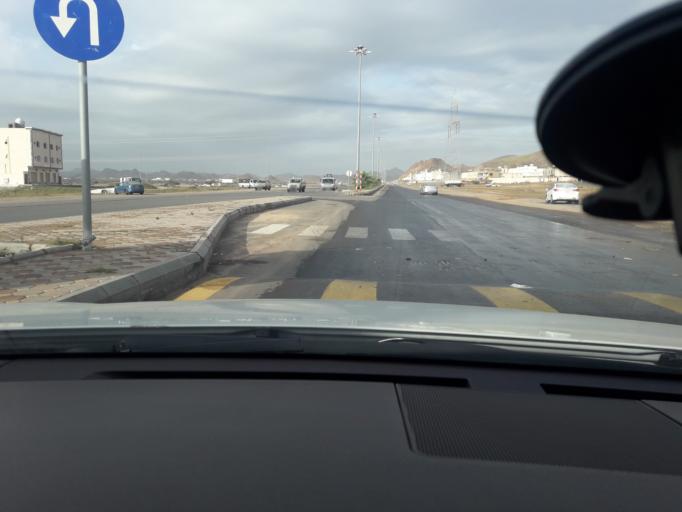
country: SA
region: Al Madinah al Munawwarah
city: Sultanah
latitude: 24.4677
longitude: 39.4904
